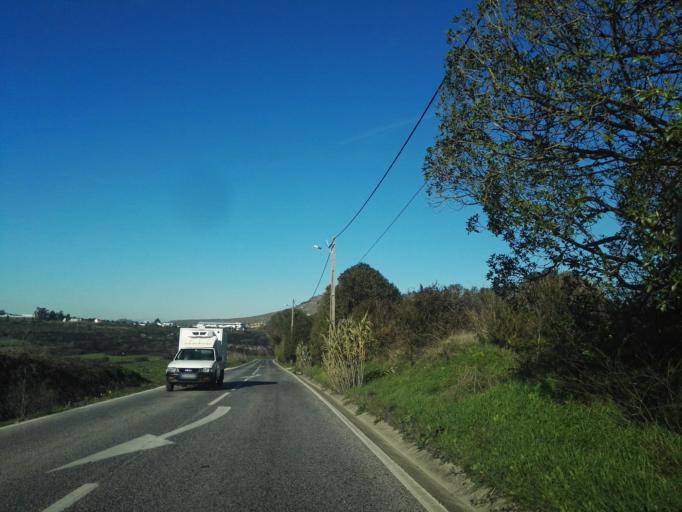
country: PT
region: Lisbon
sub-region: Loures
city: Loures
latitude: 38.8812
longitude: -9.1860
